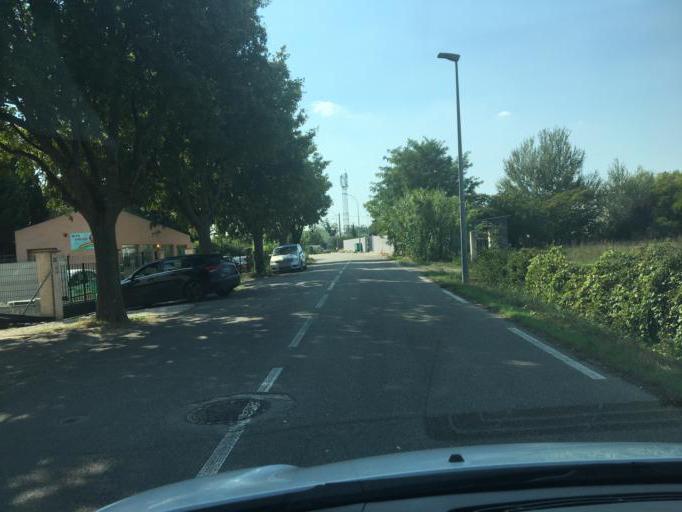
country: FR
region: Provence-Alpes-Cote d'Azur
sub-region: Departement du Vaucluse
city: Morieres-les-Avignon
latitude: 43.9521
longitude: 4.8888
